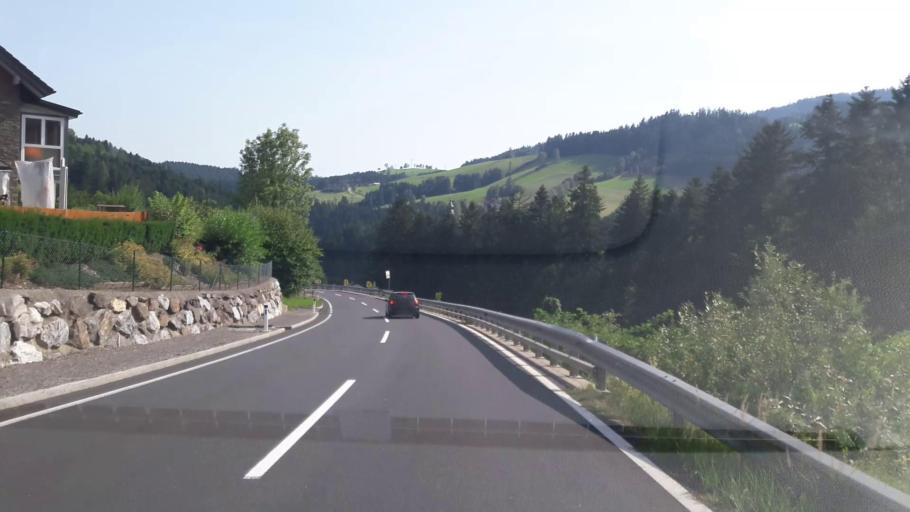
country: AT
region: Styria
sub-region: Politischer Bezirk Weiz
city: Birkfeld
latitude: 47.3454
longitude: 15.6845
